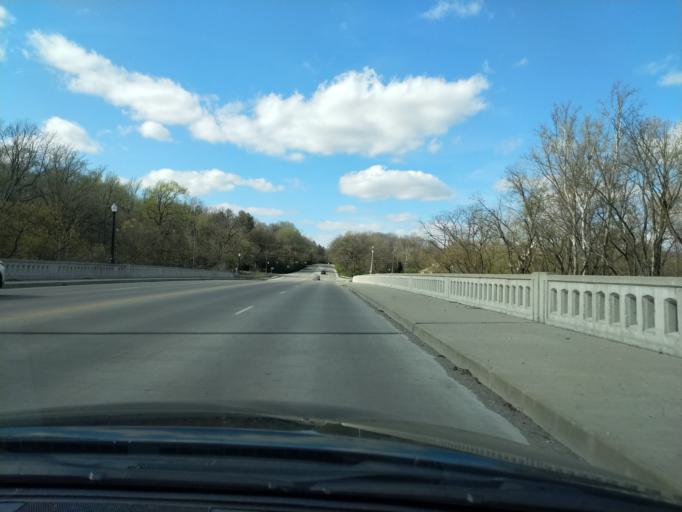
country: US
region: Indiana
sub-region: Marion County
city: Broad Ripple
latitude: 39.8717
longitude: -86.1563
